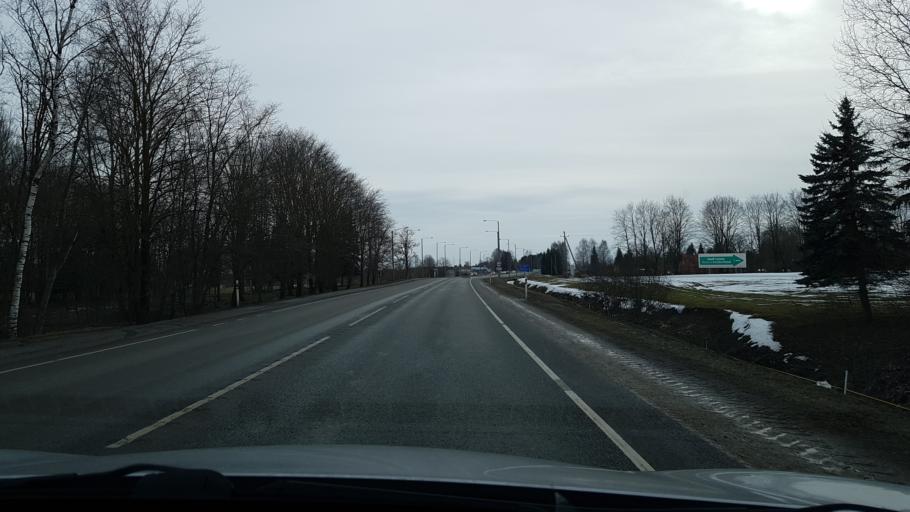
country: EE
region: Tartu
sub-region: UElenurme vald
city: Ulenurme
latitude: 58.2984
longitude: 26.7199
